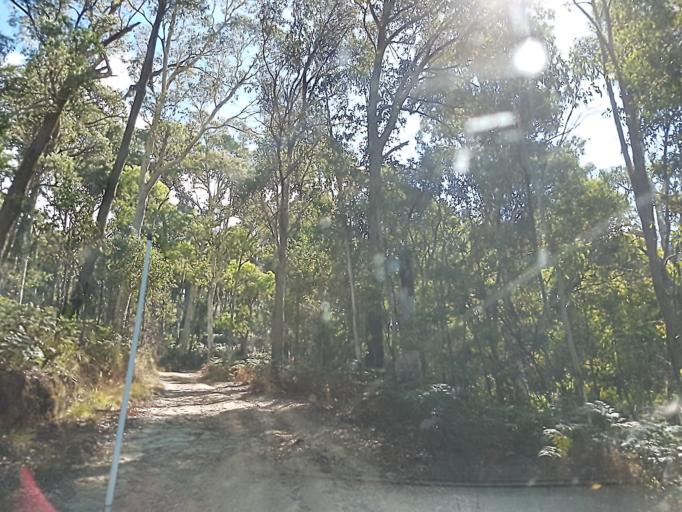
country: AU
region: Victoria
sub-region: Alpine
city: Mount Beauty
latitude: -36.8795
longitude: 147.0283
